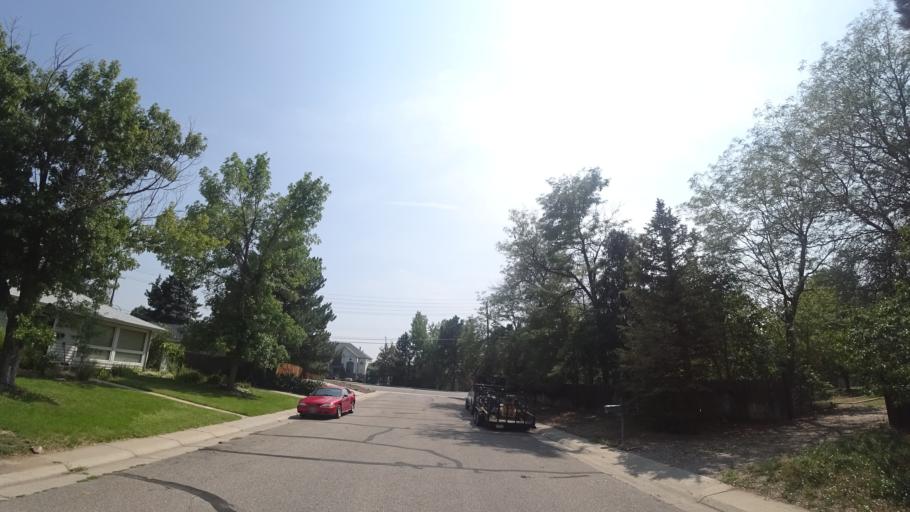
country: US
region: Colorado
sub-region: Arapahoe County
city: Littleton
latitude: 39.6246
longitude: -104.9961
